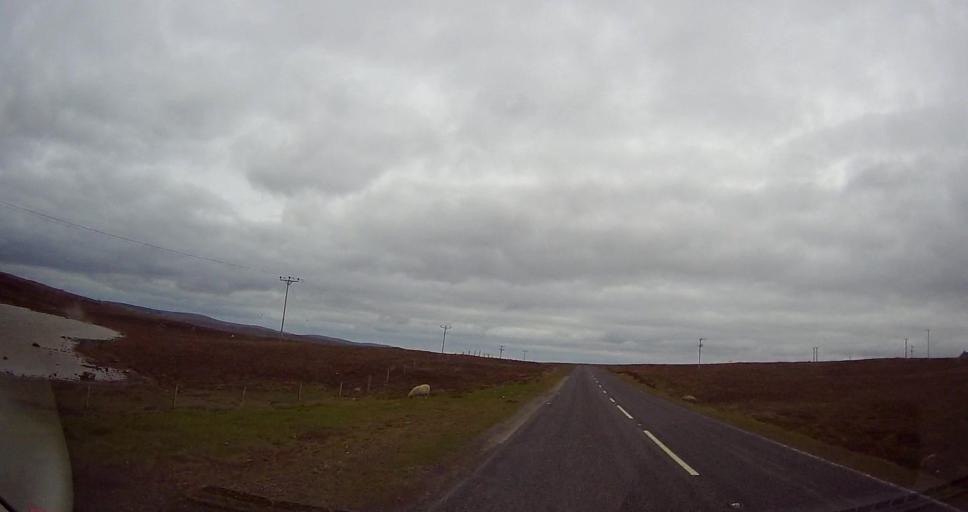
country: GB
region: Scotland
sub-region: Shetland Islands
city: Shetland
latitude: 60.7128
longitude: -0.9163
